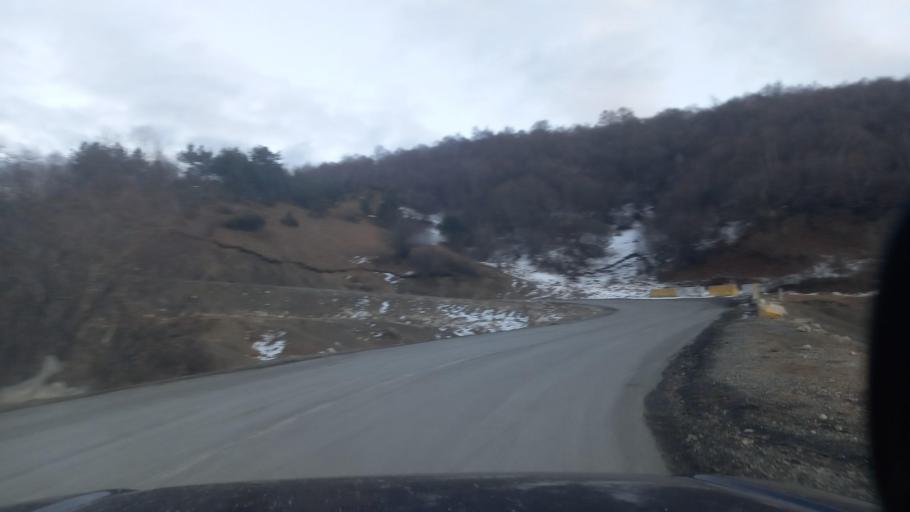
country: RU
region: Ingushetiya
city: Dzhayrakh
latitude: 42.8215
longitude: 44.8175
